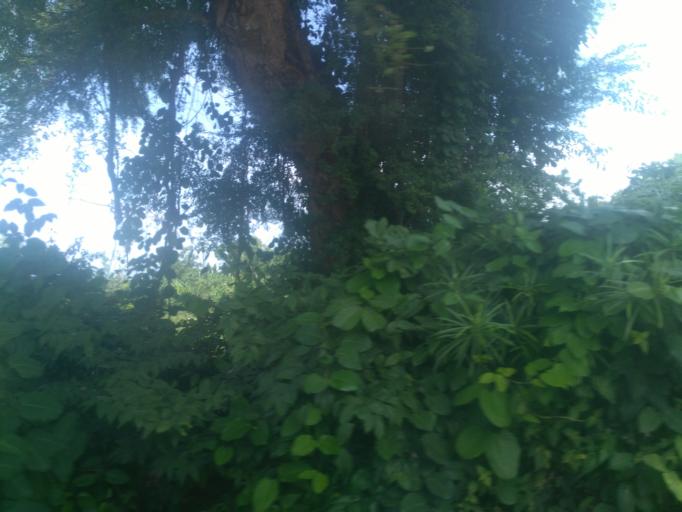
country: TZ
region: Zanzibar Urban/West
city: Zanzibar
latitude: -6.2137
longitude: 39.2111
